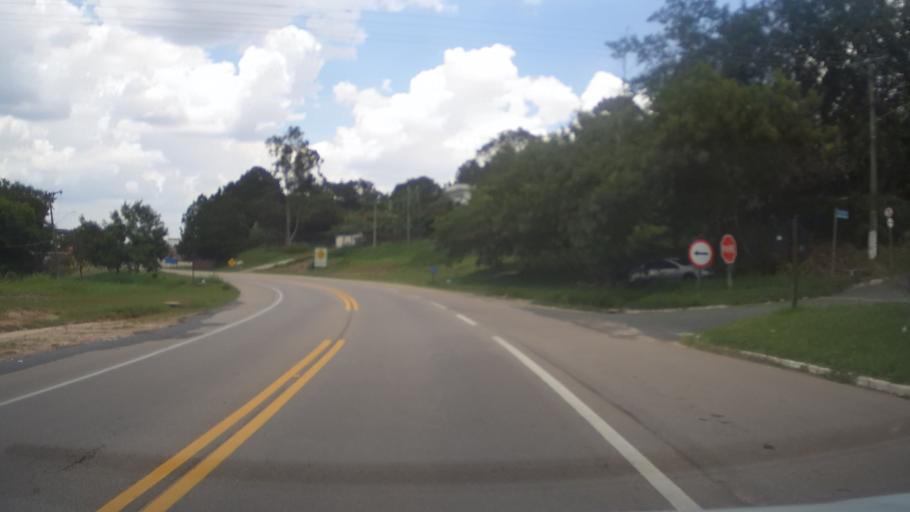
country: BR
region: Sao Paulo
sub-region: Vinhedo
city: Vinhedo
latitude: -23.0407
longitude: -46.9680
